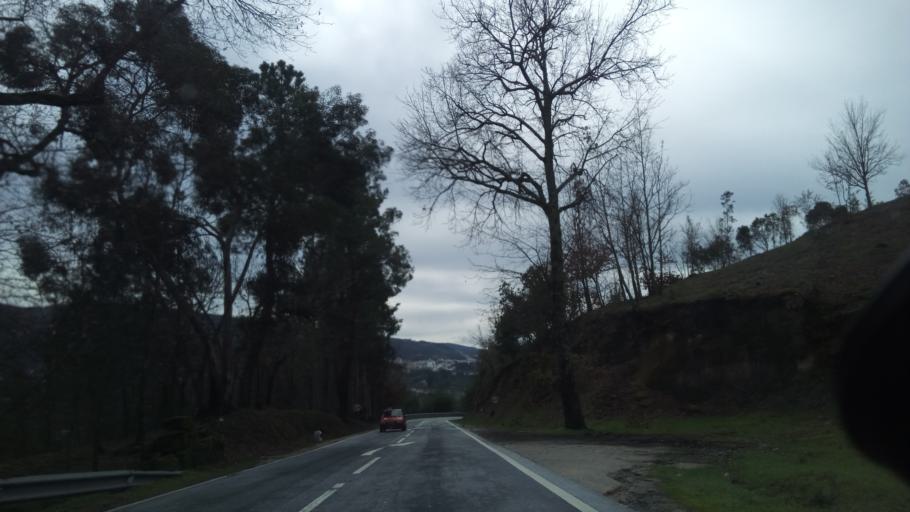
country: PT
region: Guarda
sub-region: Seia
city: Seia
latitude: 40.4406
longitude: -7.7092
